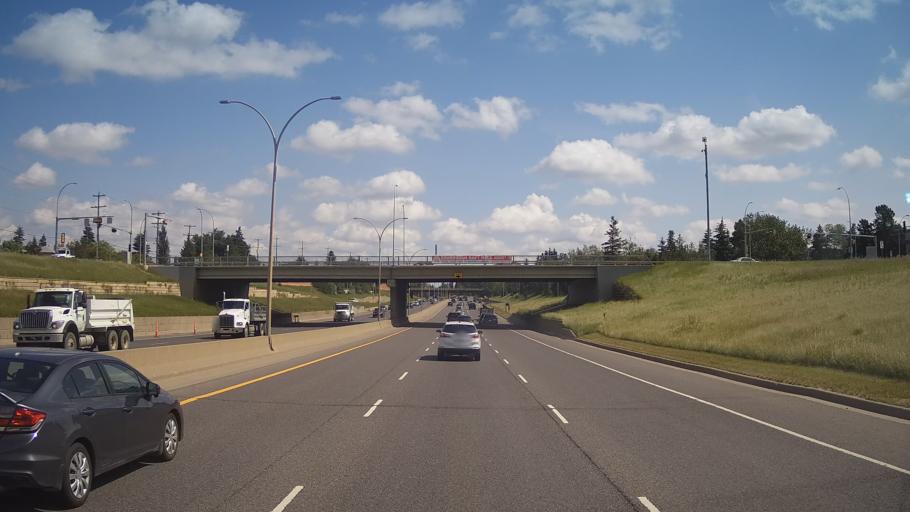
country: CA
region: Alberta
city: St. Albert
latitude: 53.5120
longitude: -113.5983
